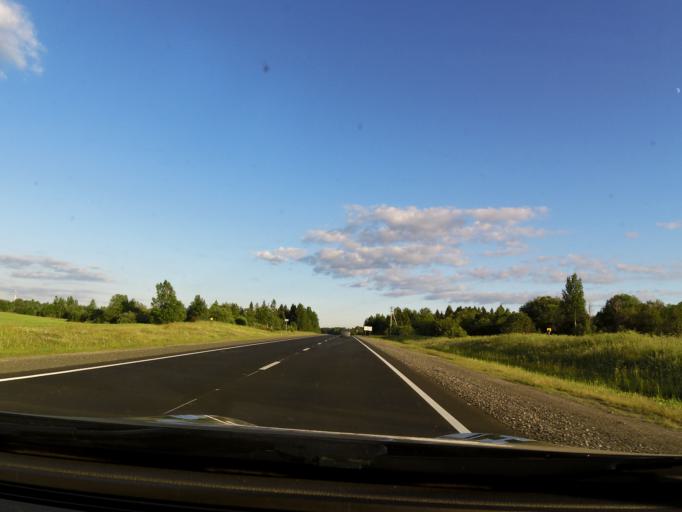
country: RU
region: Vologda
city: Gryazovets
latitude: 59.0145
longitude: 40.1191
